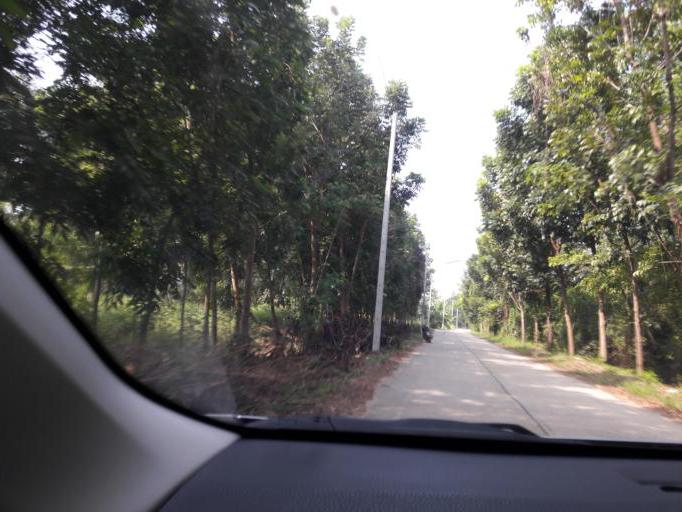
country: TH
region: Ang Thong
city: Ang Thong
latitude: 14.5496
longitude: 100.4324
